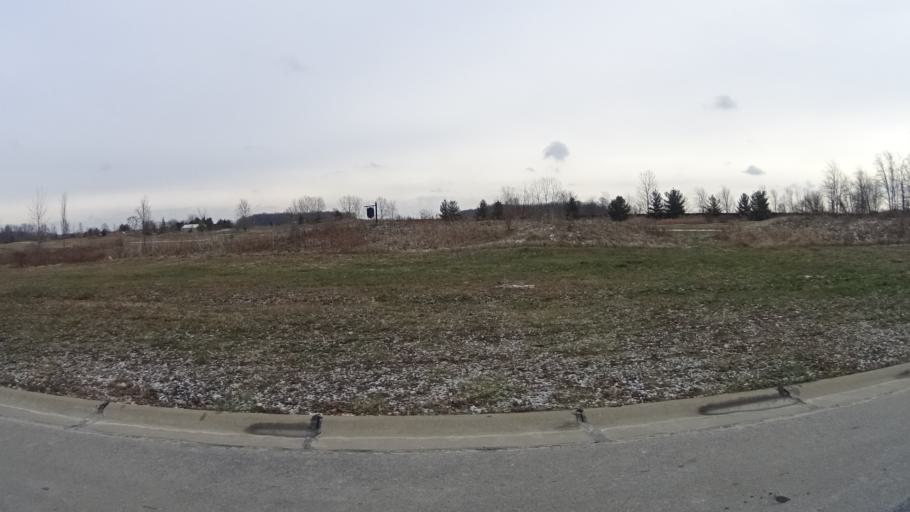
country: US
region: Ohio
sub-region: Lorain County
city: Lagrange
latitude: 41.2458
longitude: -82.1064
